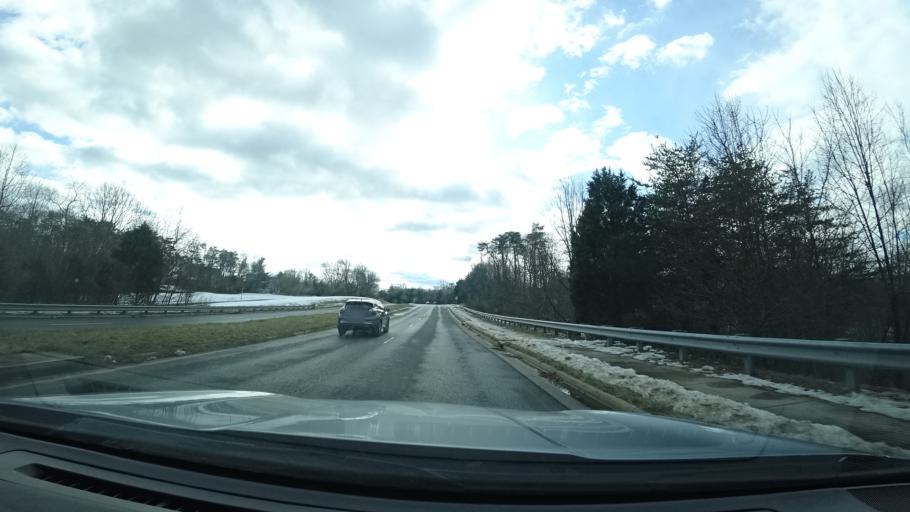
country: US
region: Virginia
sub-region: Loudoun County
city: Sugarland Run
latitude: 39.0273
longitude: -77.3635
